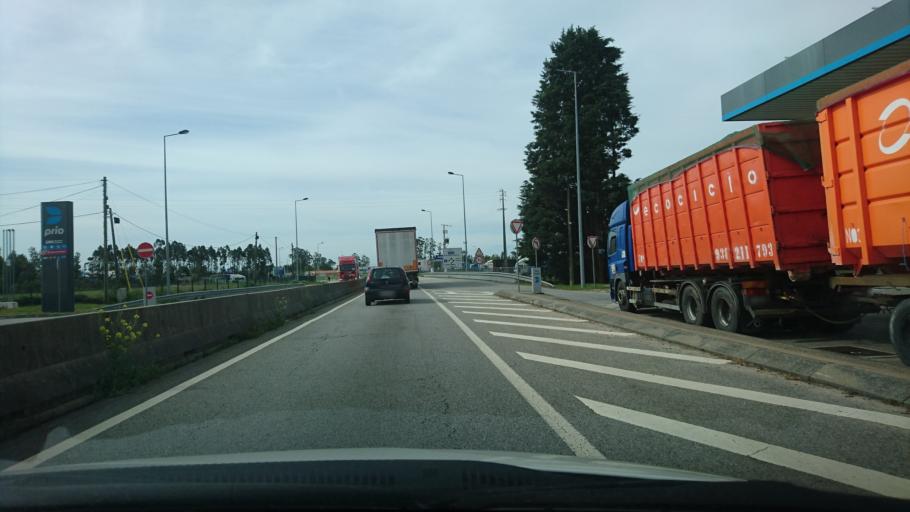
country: PT
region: Aveiro
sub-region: Albergaria-A-Velha
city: Albergaria-a-Velha
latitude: 40.7085
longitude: -8.4831
